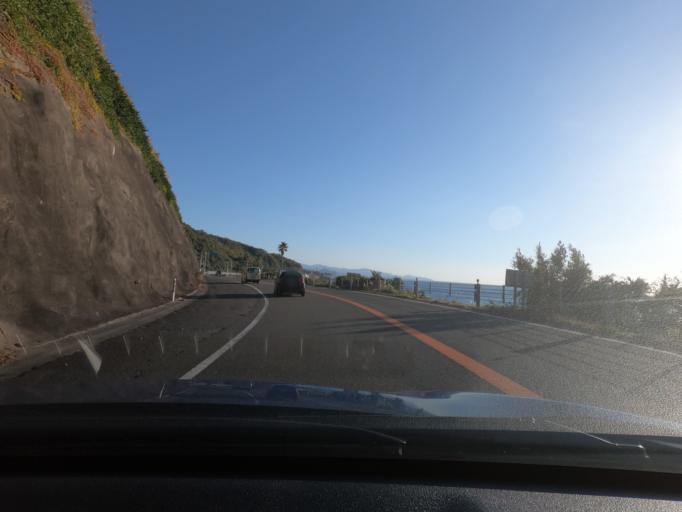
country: JP
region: Kagoshima
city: Akune
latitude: 31.9508
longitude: 130.2158
